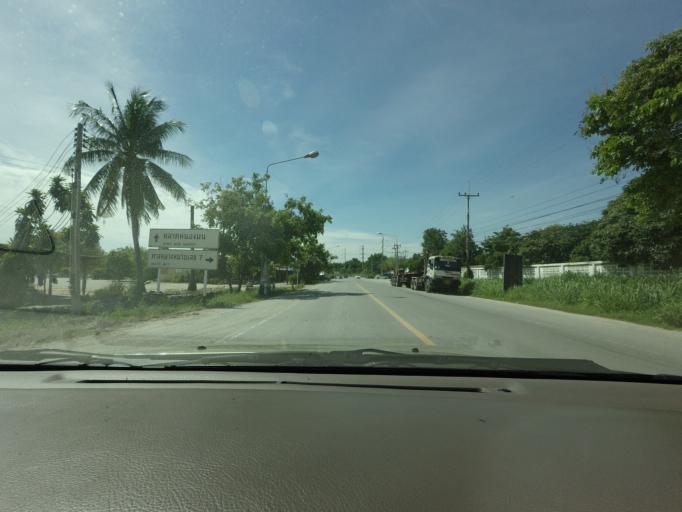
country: TH
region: Chon Buri
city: Chon Buri
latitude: 13.2762
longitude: 100.9656
